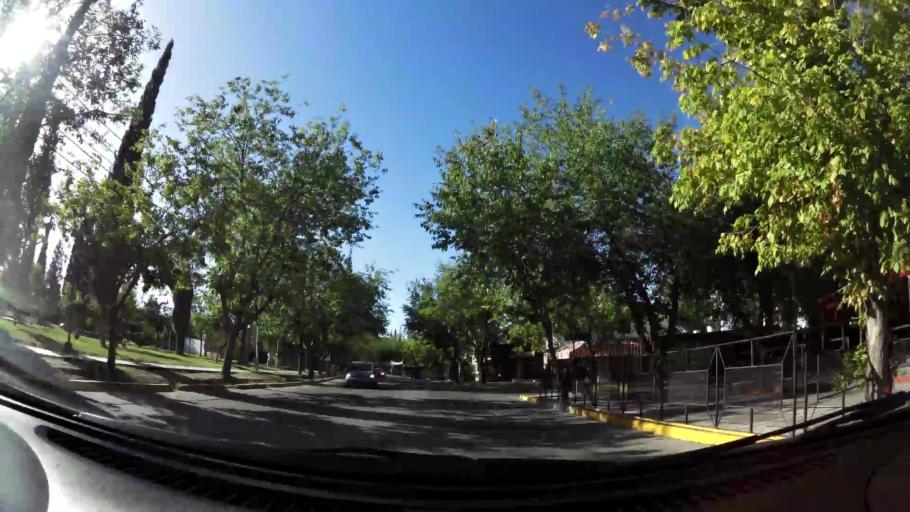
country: AR
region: Mendoza
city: Villa Nueva
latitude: -32.9056
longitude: -68.8002
